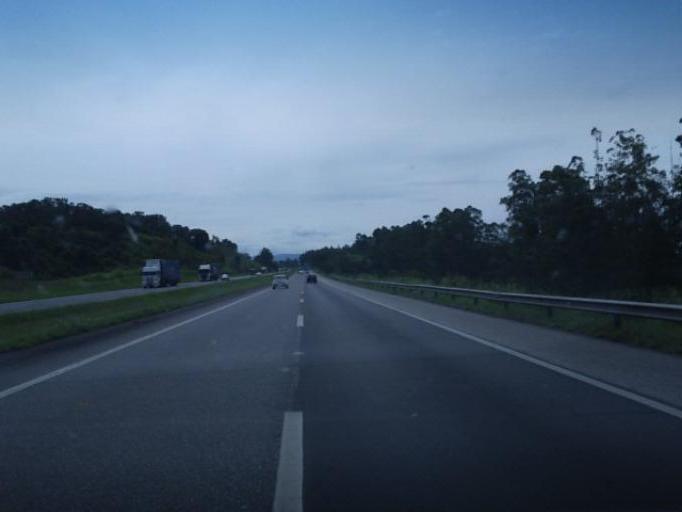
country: BR
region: Sao Paulo
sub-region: Cajati
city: Cajati
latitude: -24.7217
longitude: -48.0707
